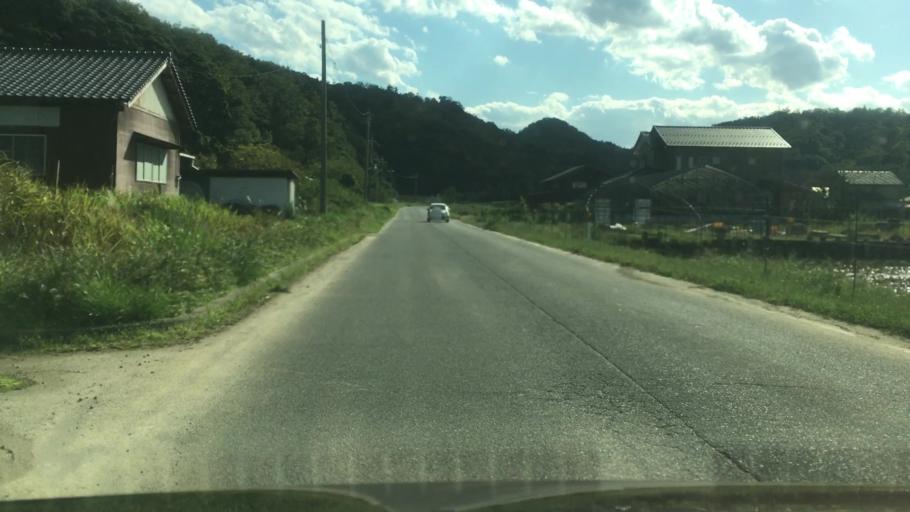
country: JP
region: Hyogo
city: Toyooka
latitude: 35.6486
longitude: 134.9654
